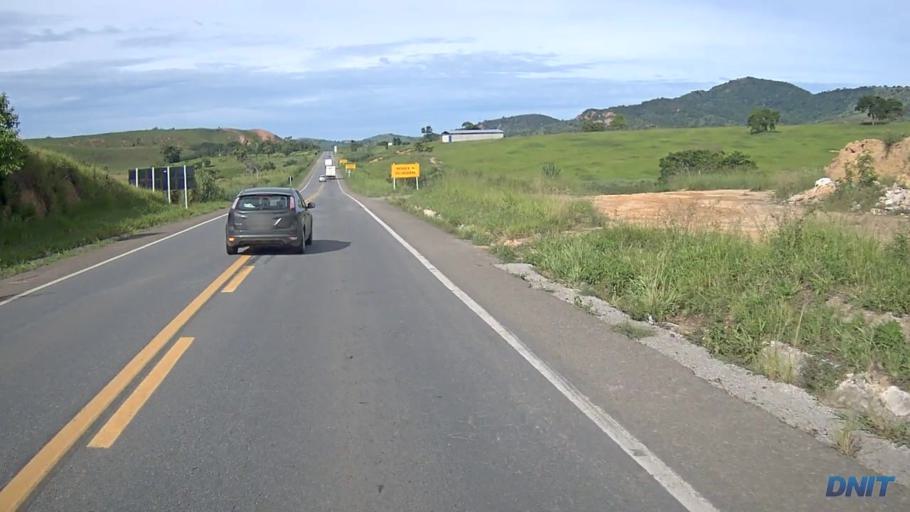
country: BR
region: Minas Gerais
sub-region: Belo Oriente
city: Belo Oriente
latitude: -19.1932
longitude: -42.2771
